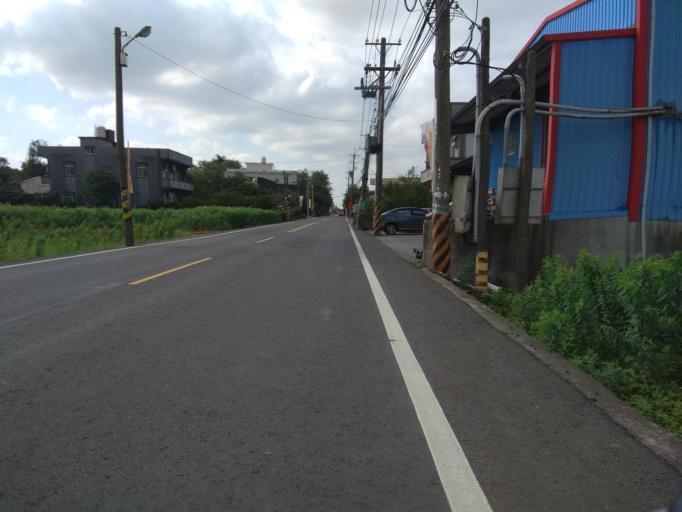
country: TW
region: Taiwan
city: Taoyuan City
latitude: 25.0660
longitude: 121.2409
